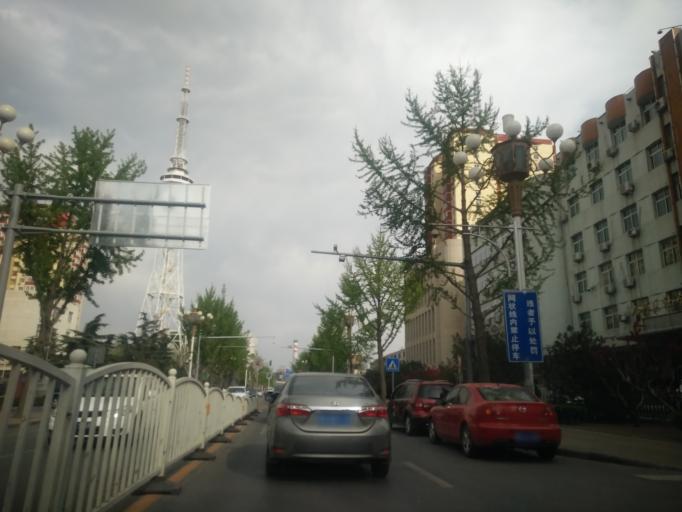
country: CN
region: Beijing
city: Xingfeng
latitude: 39.7254
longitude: 116.3348
